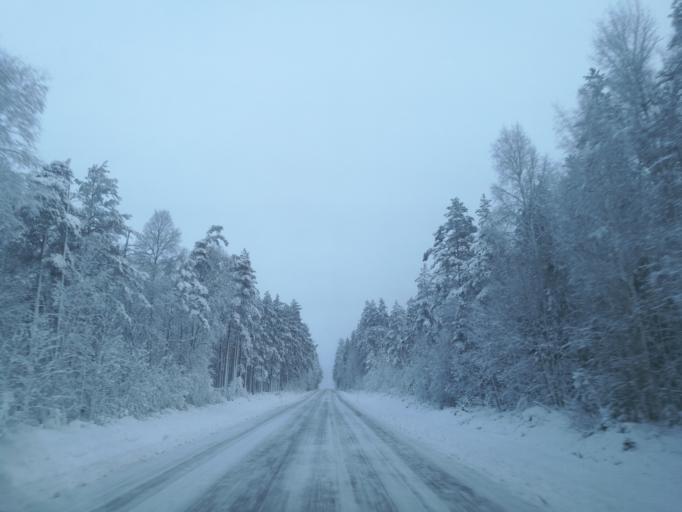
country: NO
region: Hedmark
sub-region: Grue
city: Kirkenaer
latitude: 60.4786
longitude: 12.5583
